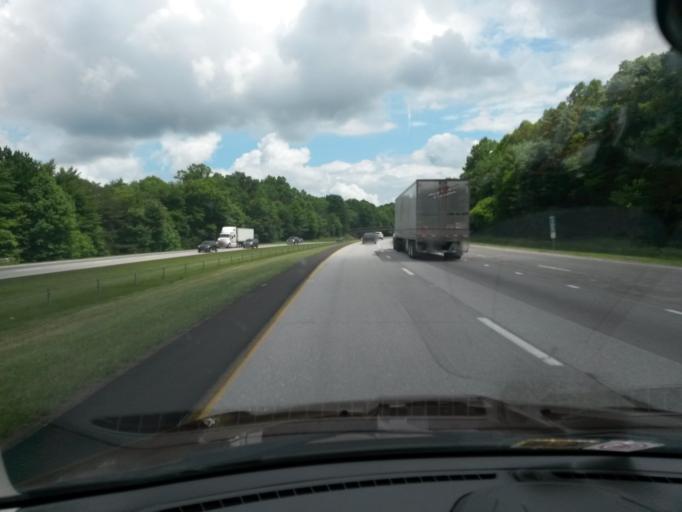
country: US
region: Virginia
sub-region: Carroll County
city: Cana
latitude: 36.5564
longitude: -80.7431
